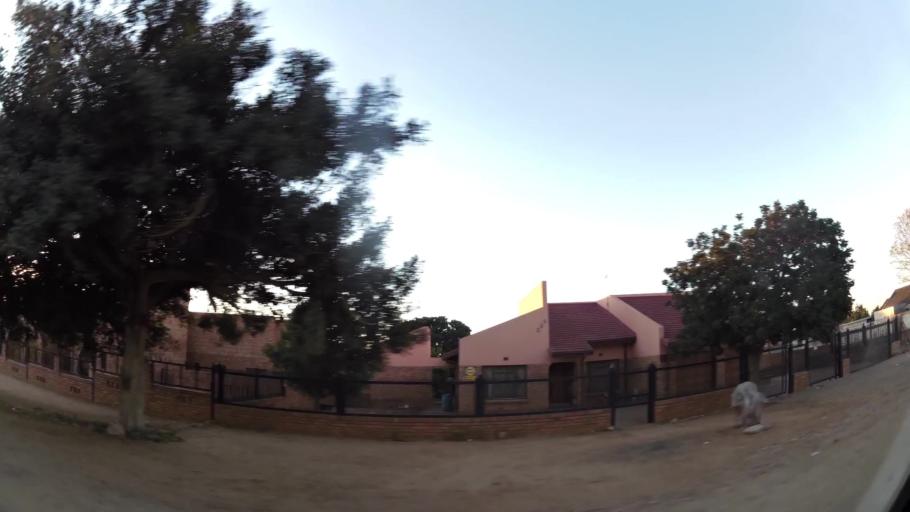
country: ZA
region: Limpopo
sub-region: Capricorn District Municipality
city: Polokwane
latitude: -23.8536
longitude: 29.3658
